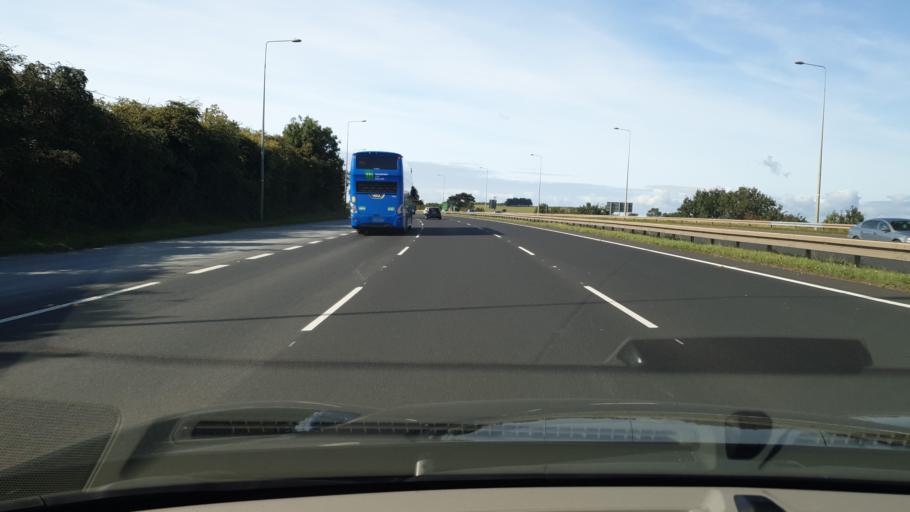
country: IE
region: Leinster
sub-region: South Dublin
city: Newcastle
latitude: 53.2767
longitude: -6.5032
